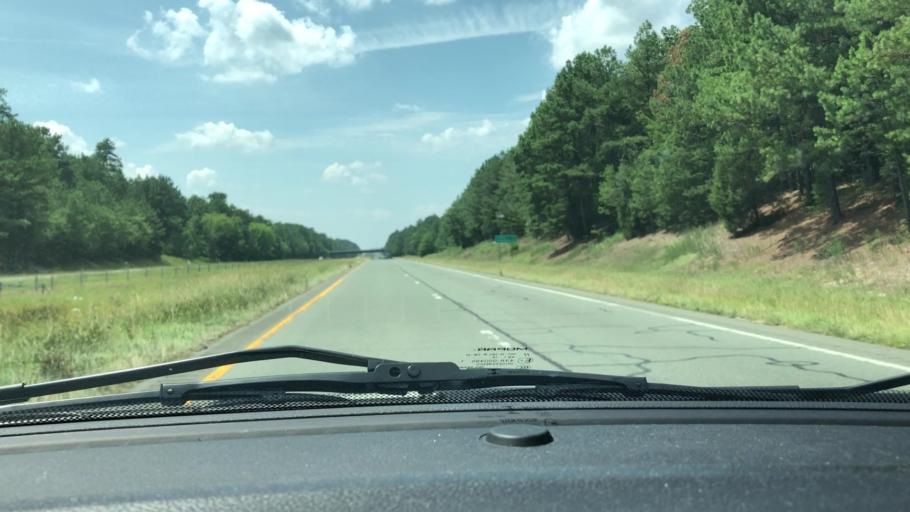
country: US
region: North Carolina
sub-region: Chatham County
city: Siler City
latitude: 35.7491
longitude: -79.4475
